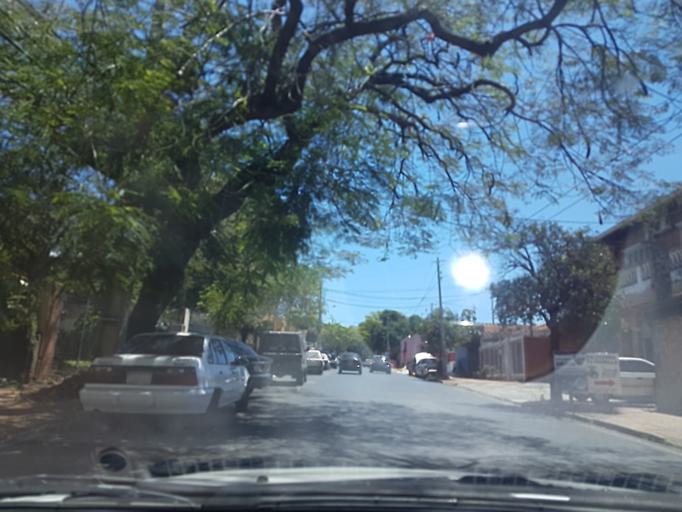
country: PY
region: Asuncion
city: Asuncion
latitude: -25.3060
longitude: -57.5974
